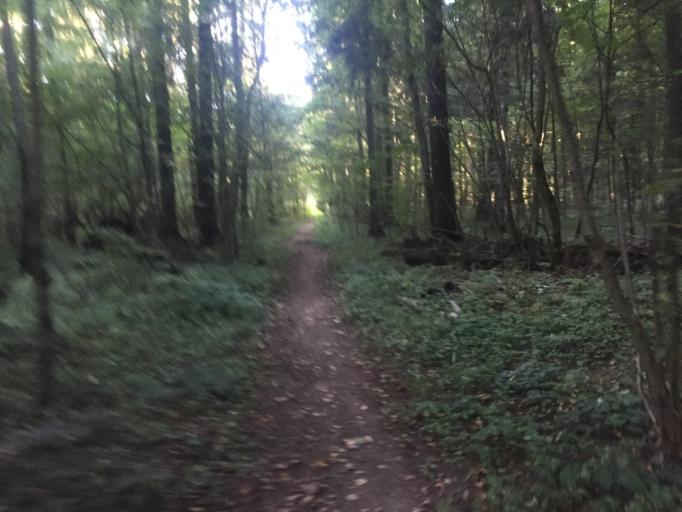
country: RU
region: Moscow
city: Gol'yanovo
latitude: 55.8471
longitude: 37.7875
